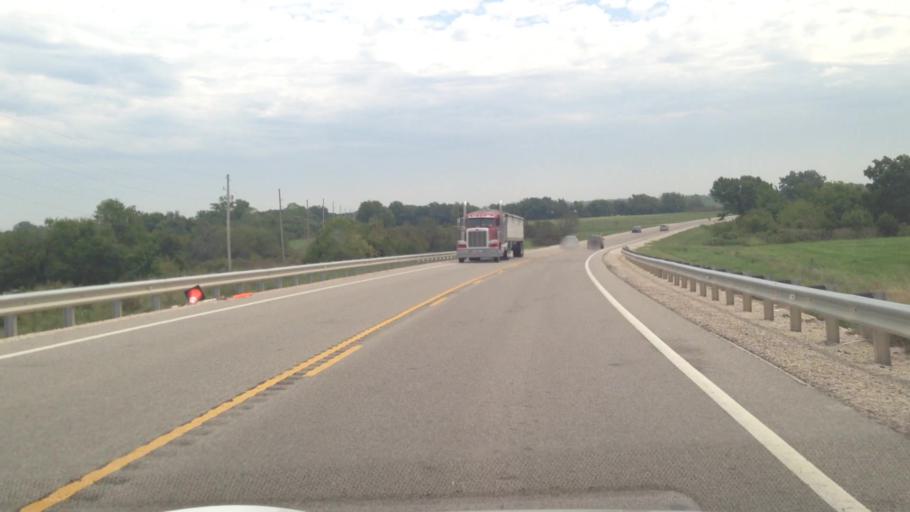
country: US
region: Kansas
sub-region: Allen County
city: Iola
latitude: 37.9215
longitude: -95.1625
